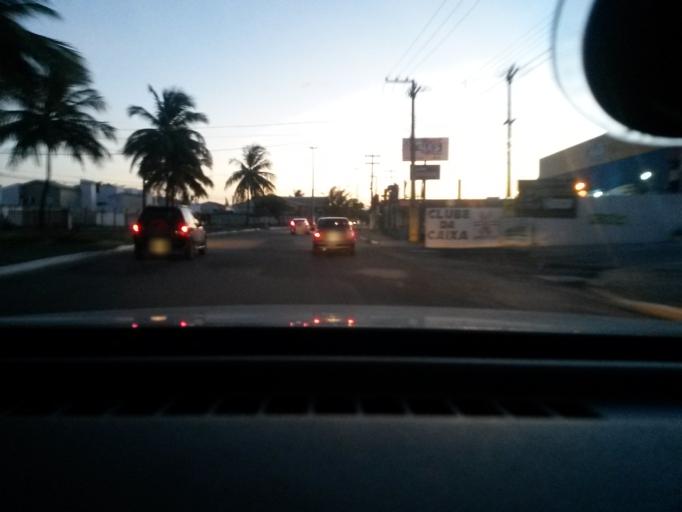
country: BR
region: Sergipe
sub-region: Aracaju
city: Aracaju
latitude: -10.9939
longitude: -37.0638
